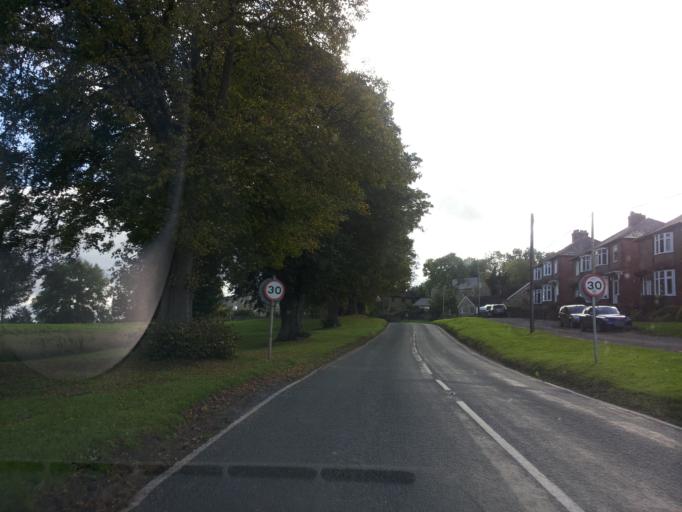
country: GB
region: England
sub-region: North Yorkshire
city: Leyburn
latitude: 54.2890
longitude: -1.8091
